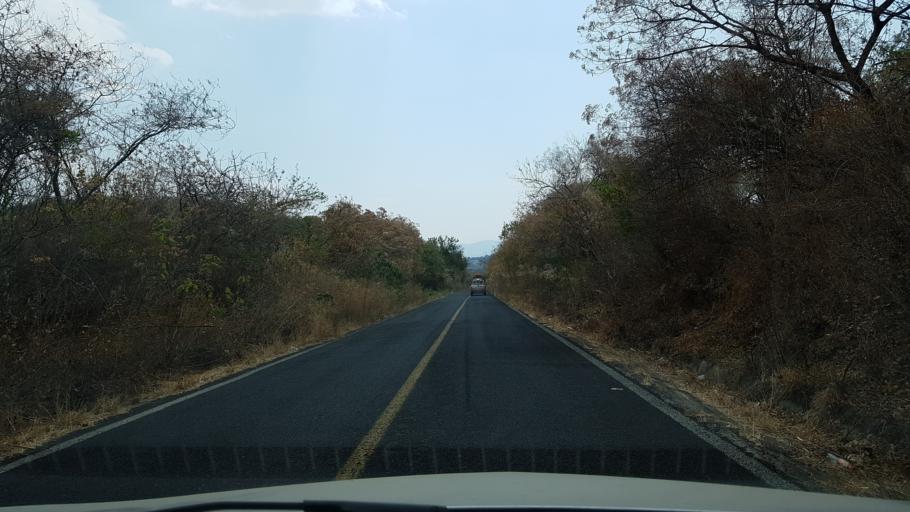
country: MX
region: Morelos
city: Tlacotepec
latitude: 18.8373
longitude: -98.7325
